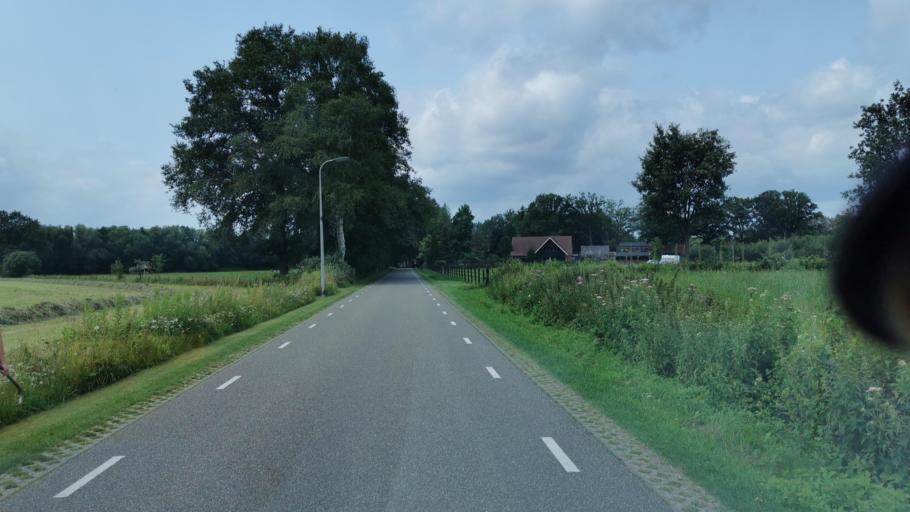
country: NL
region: Overijssel
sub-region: Gemeente Losser
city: Losser
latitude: 52.2331
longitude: 6.9558
